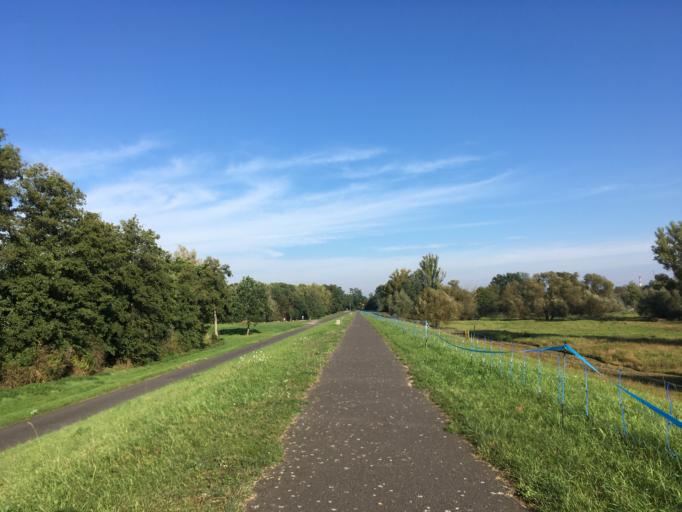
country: PL
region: Lubusz
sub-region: Powiat gorzowski
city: Kostrzyn nad Odra
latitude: 52.5675
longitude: 14.6223
